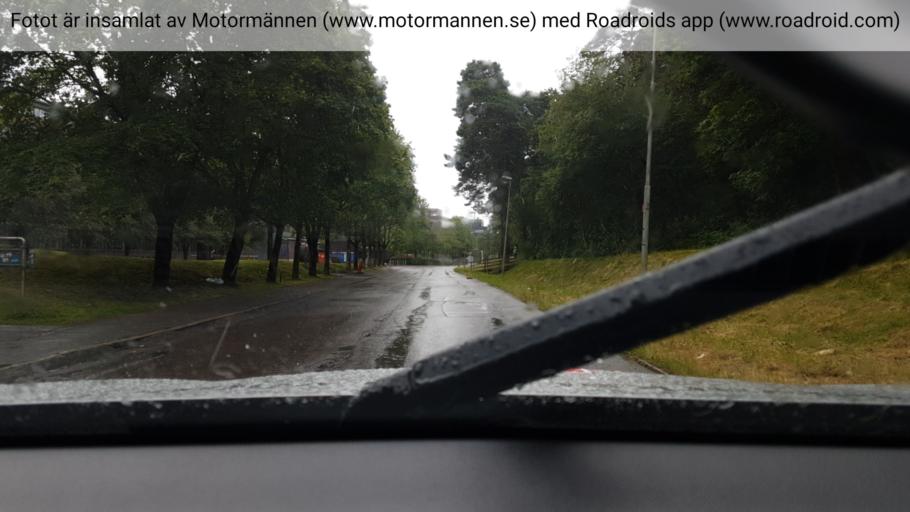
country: SE
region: Vaestra Goetaland
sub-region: Goteborg
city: Goeteborg
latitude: 57.6884
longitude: 11.9745
